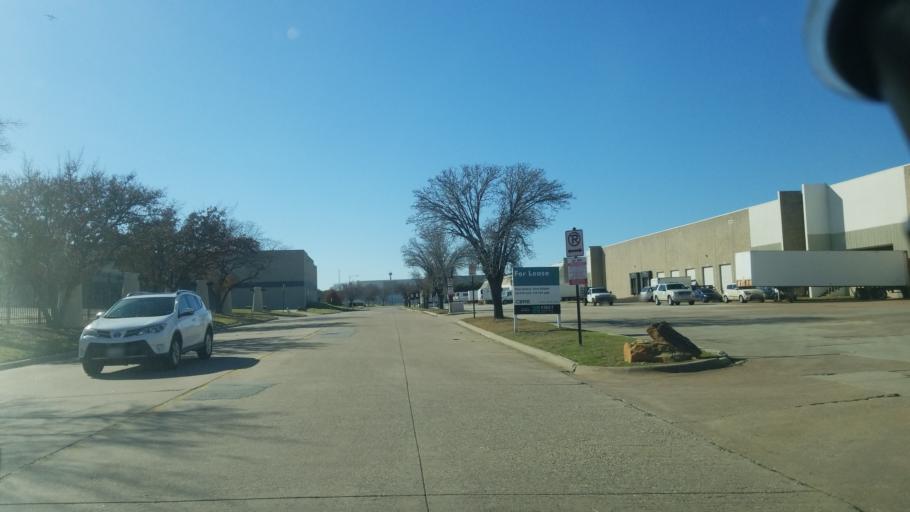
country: US
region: Texas
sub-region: Tarrant County
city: Arlington
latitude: 32.7462
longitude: -97.0652
